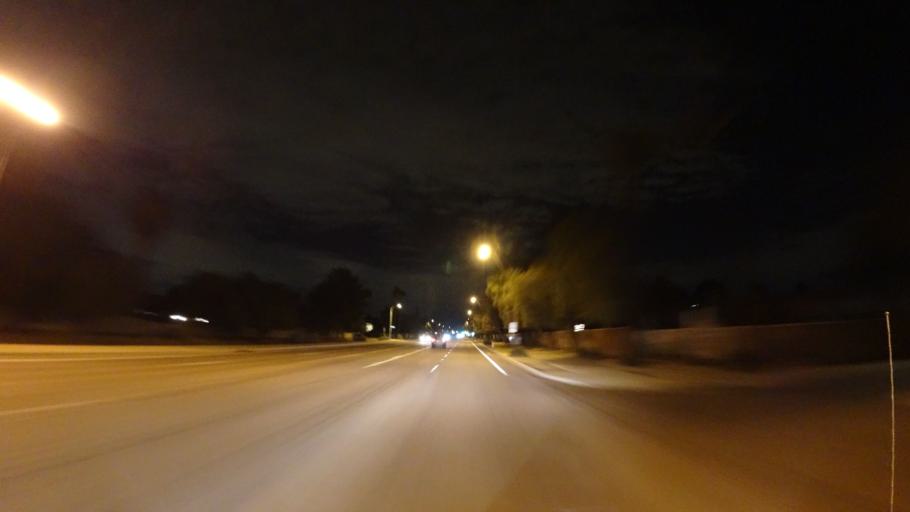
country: US
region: Arizona
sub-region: Maricopa County
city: San Carlos
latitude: 33.3294
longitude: -111.9111
